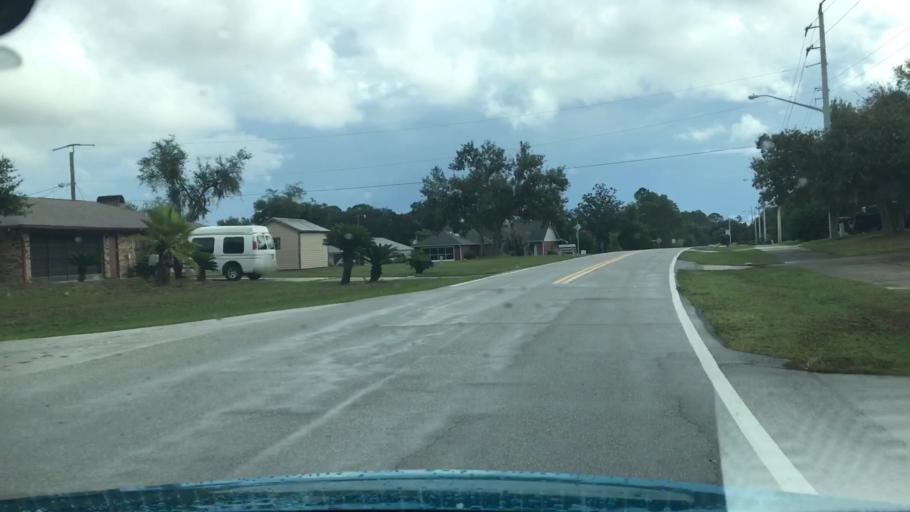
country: US
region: Florida
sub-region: Volusia County
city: Deltona
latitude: 28.9206
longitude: -81.2024
